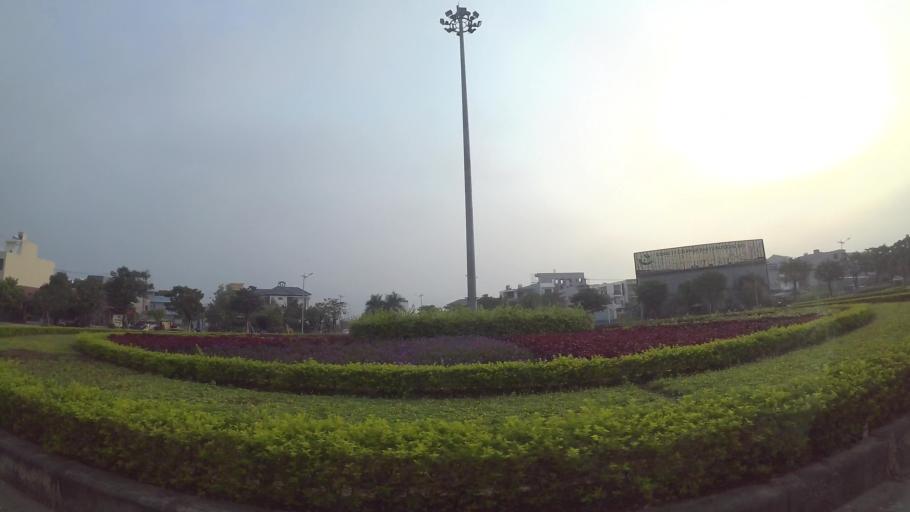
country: VN
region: Da Nang
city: Ngu Hanh Son
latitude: 16.0184
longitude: 108.2299
